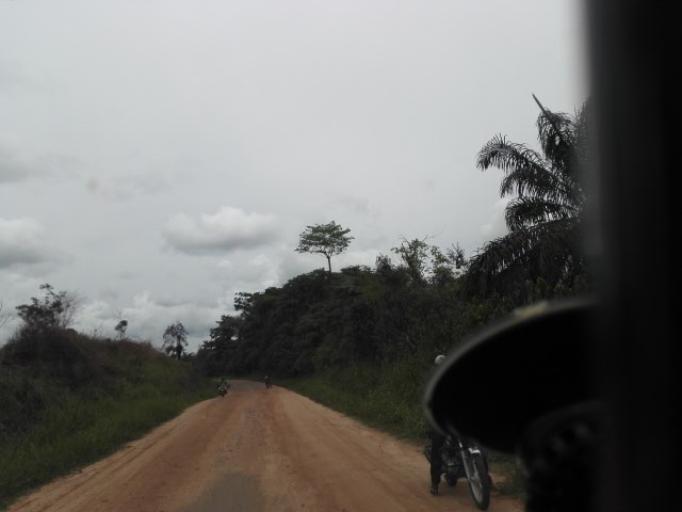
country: CD
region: Eastern Province
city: Kisangani
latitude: 0.4622
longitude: 25.3516
